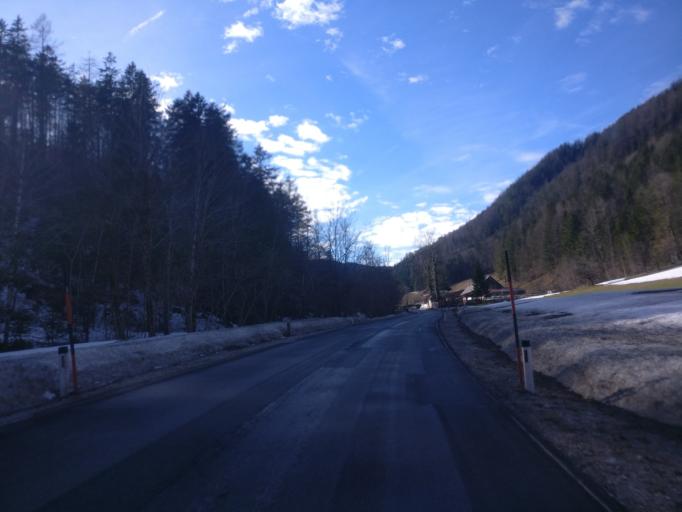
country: AT
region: Styria
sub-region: Politischer Bezirk Liezen
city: Landl
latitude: 47.6522
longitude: 14.6880
